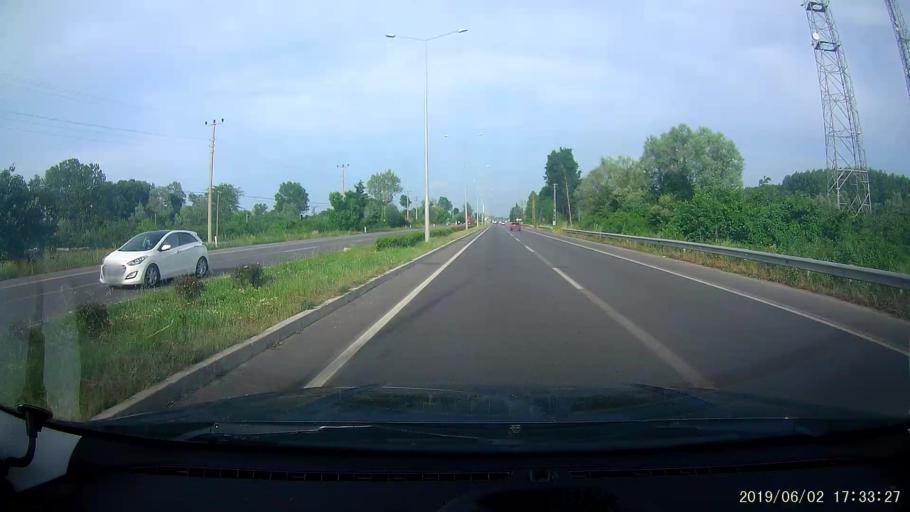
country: TR
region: Samsun
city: Terme
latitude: 41.2208
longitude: 36.8490
